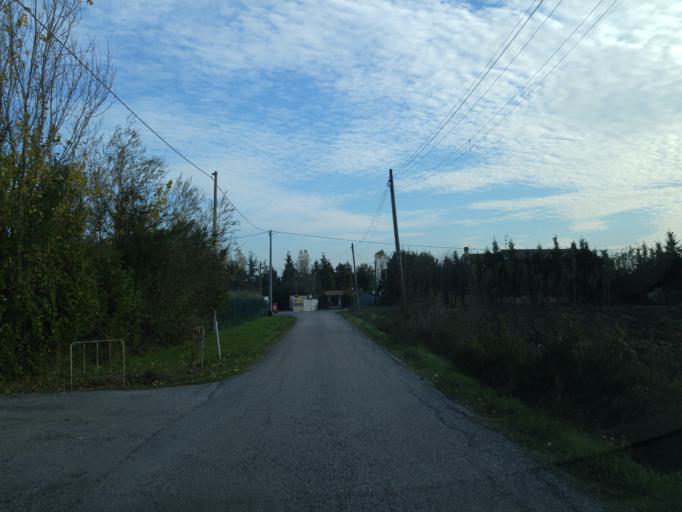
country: IT
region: The Marches
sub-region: Provincia di Pesaro e Urbino
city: Cuccurano
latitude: 43.7877
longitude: 12.9622
